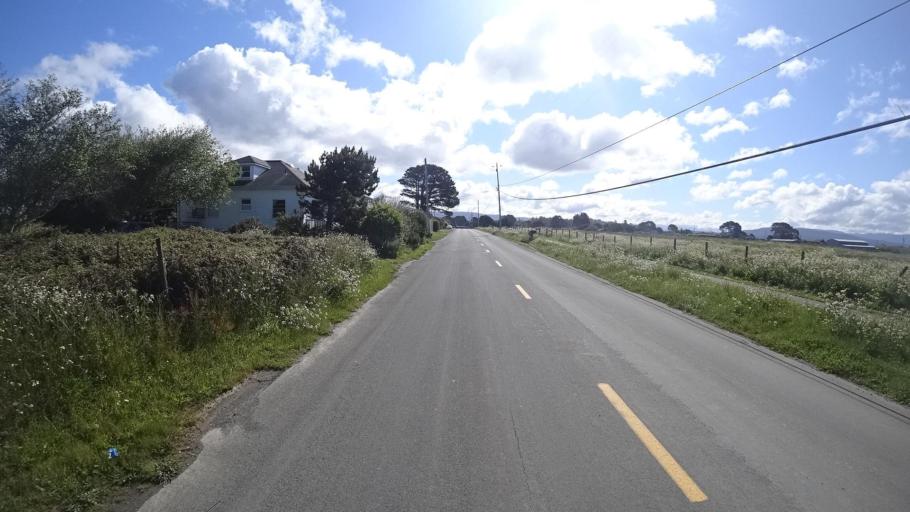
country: US
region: California
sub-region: Humboldt County
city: McKinleyville
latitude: 40.9339
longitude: -124.1240
